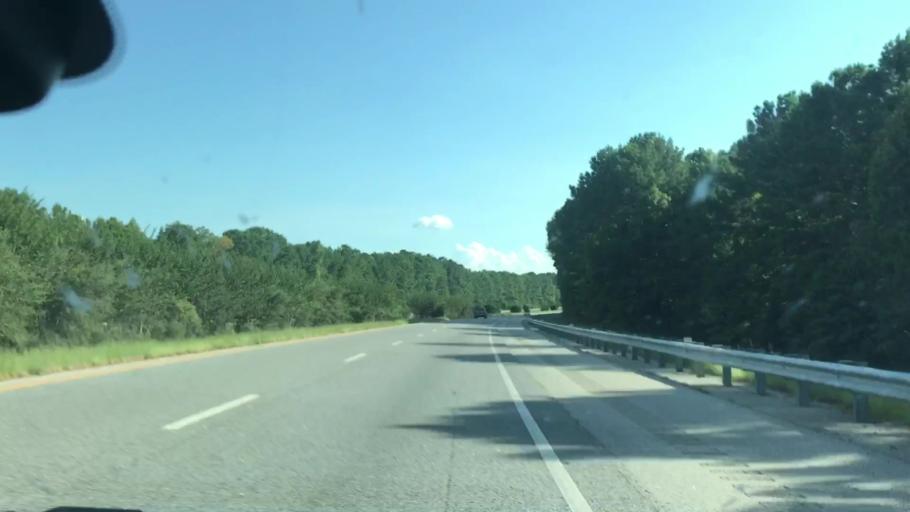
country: US
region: Georgia
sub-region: Harris County
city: Pine Mountain
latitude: 32.9041
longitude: -84.9480
